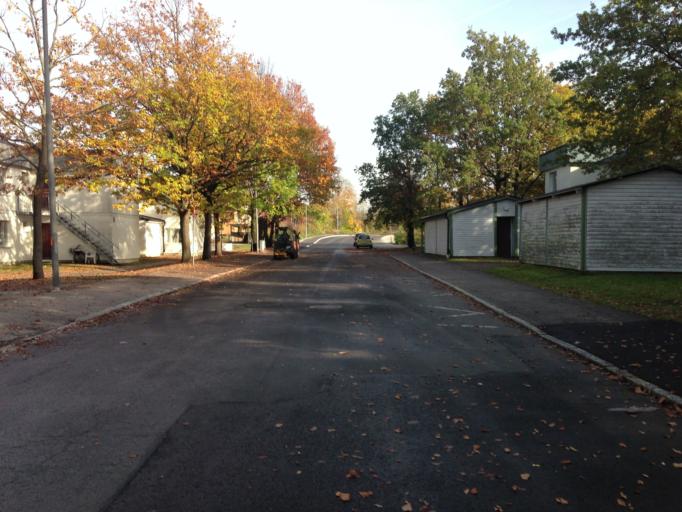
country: SE
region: Skane
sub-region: Lunds Kommun
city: Lund
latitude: 55.7216
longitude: 13.2208
